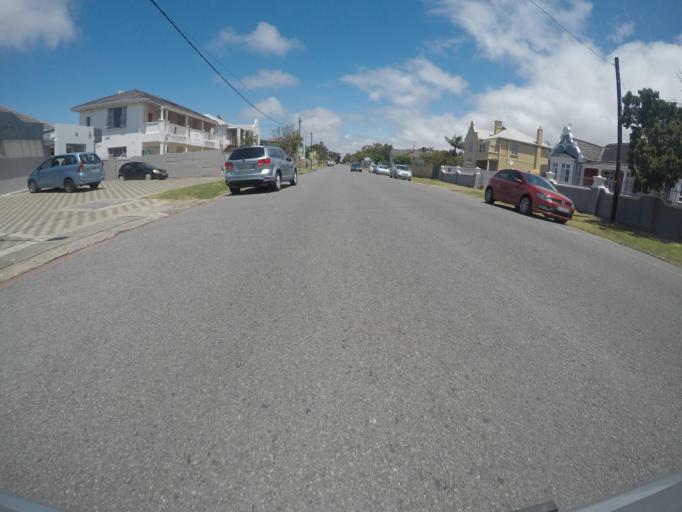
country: ZA
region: Eastern Cape
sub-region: Buffalo City Metropolitan Municipality
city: East London
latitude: -32.9986
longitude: 27.9022
